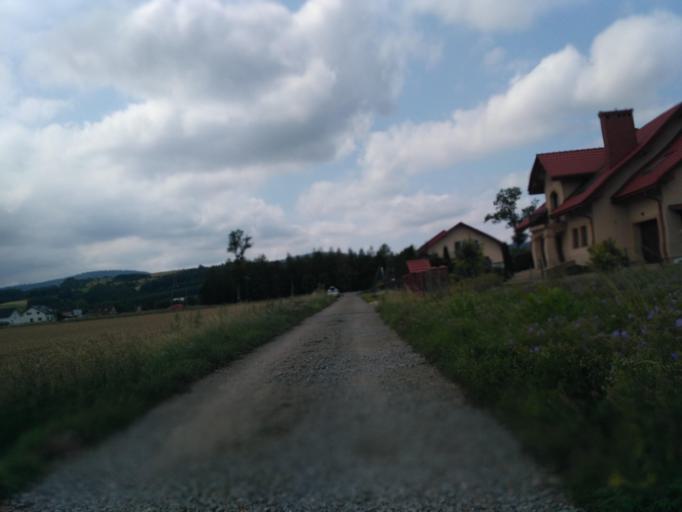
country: PL
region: Subcarpathian Voivodeship
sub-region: Powiat krosnienski
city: Rymanow
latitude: 49.5885
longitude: 21.8388
